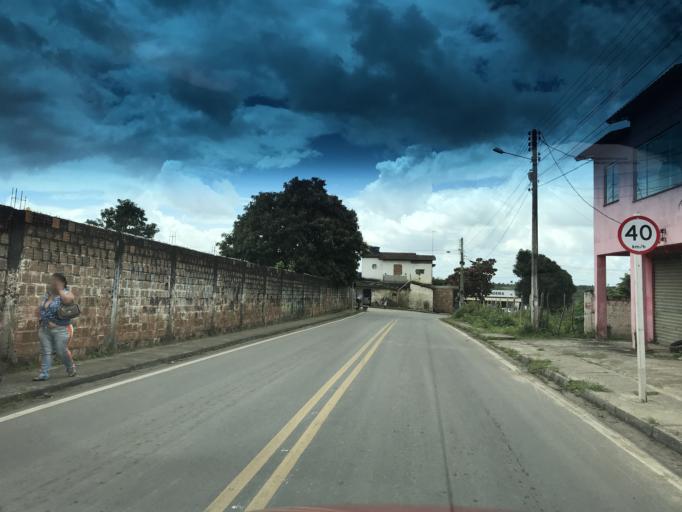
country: BR
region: Bahia
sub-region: Conceicao Do Almeida
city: Conceicao do Almeida
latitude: -12.7367
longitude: -39.1857
